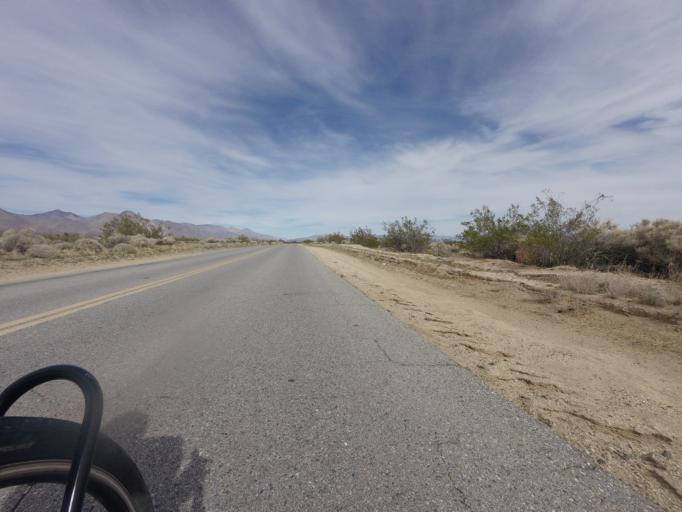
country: US
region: California
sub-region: Kern County
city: Inyokern
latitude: 35.7128
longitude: -117.8323
